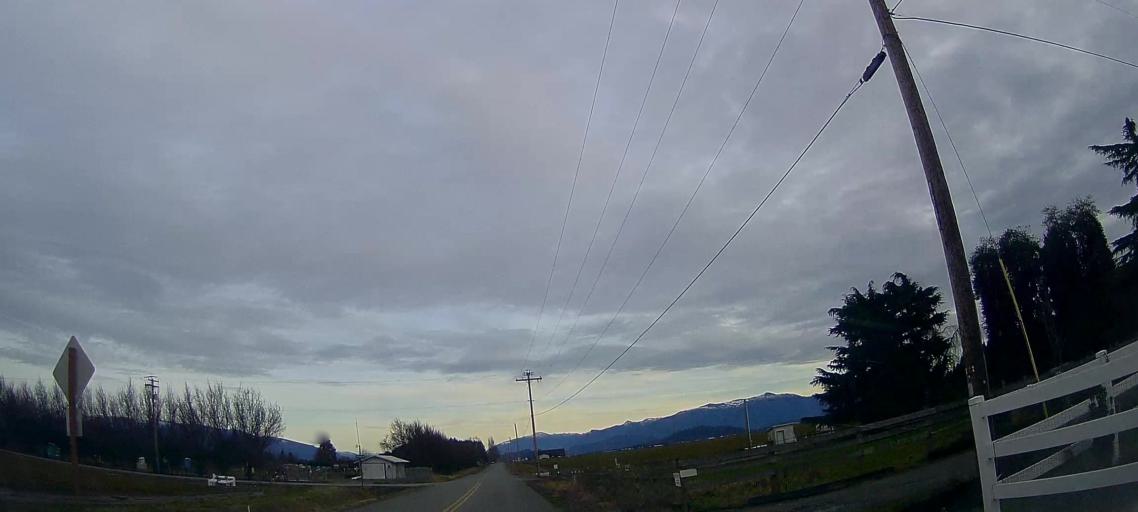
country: US
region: Washington
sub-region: Skagit County
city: Burlington
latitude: 48.5013
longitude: -122.4125
